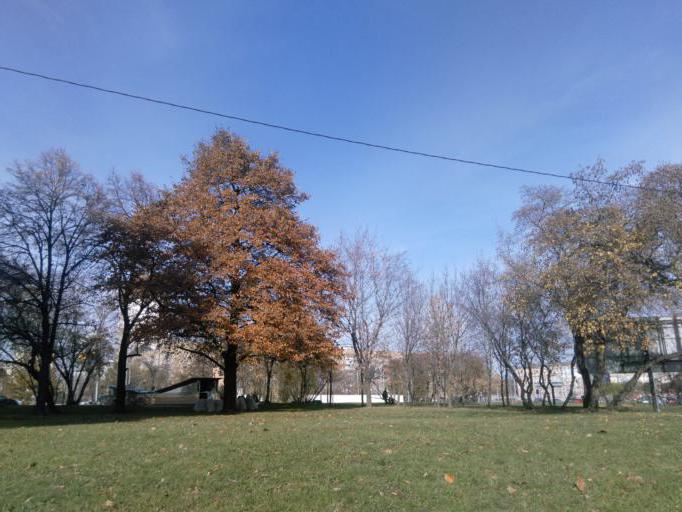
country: RU
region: Moscow
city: Novyye Cheremushki
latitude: 55.7063
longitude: 37.5803
